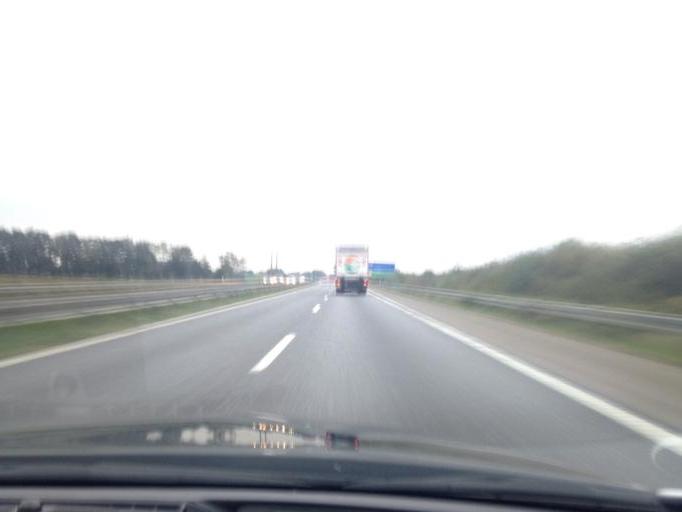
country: DK
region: South Denmark
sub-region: Haderslev Kommune
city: Haderslev
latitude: 55.2796
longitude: 9.4279
